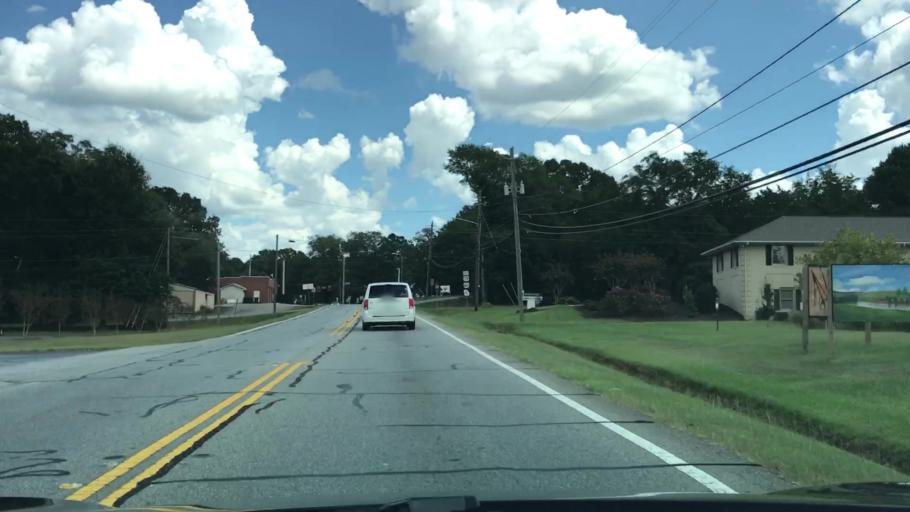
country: US
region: Georgia
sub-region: Oconee County
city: Watkinsville
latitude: 33.8661
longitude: -83.4132
